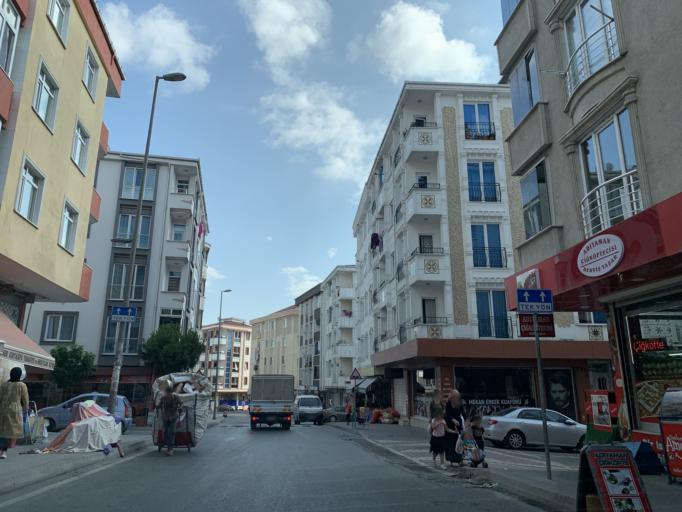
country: TR
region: Istanbul
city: Esenyurt
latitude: 41.0352
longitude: 28.6747
